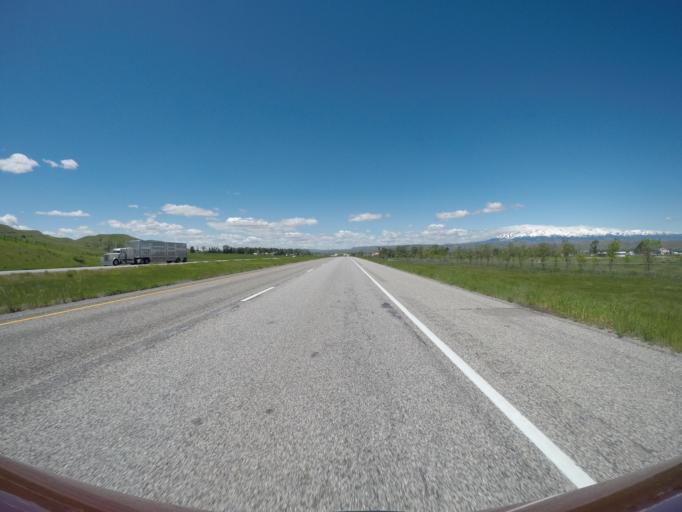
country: US
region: Montana
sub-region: Sweet Grass County
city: Big Timber
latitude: 45.8262
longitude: -109.9560
